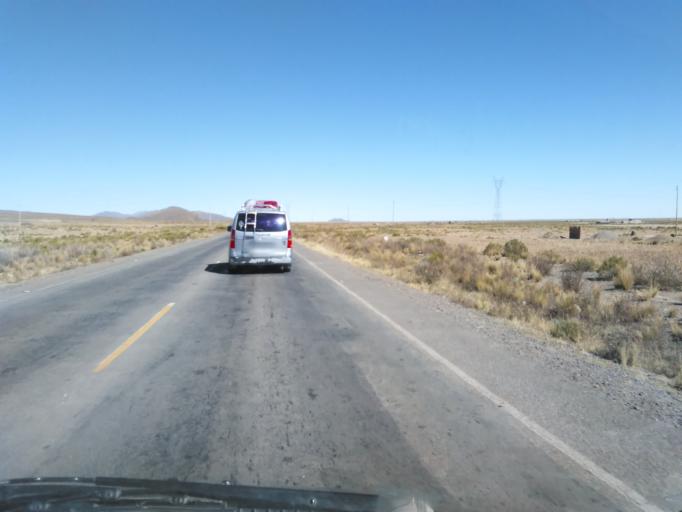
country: BO
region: Oruro
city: Machacamarca
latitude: -18.0701
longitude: -67.0057
